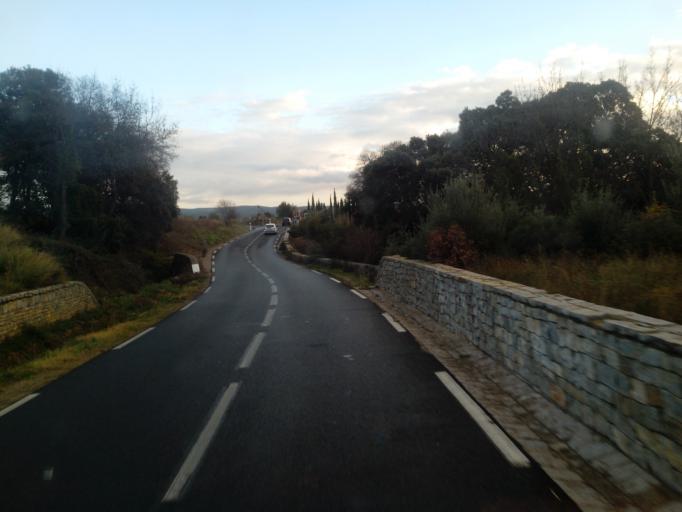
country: FR
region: Languedoc-Roussillon
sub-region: Departement de l'Herault
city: Saint-Jean-de-Fos
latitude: 43.7067
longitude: 3.5599
